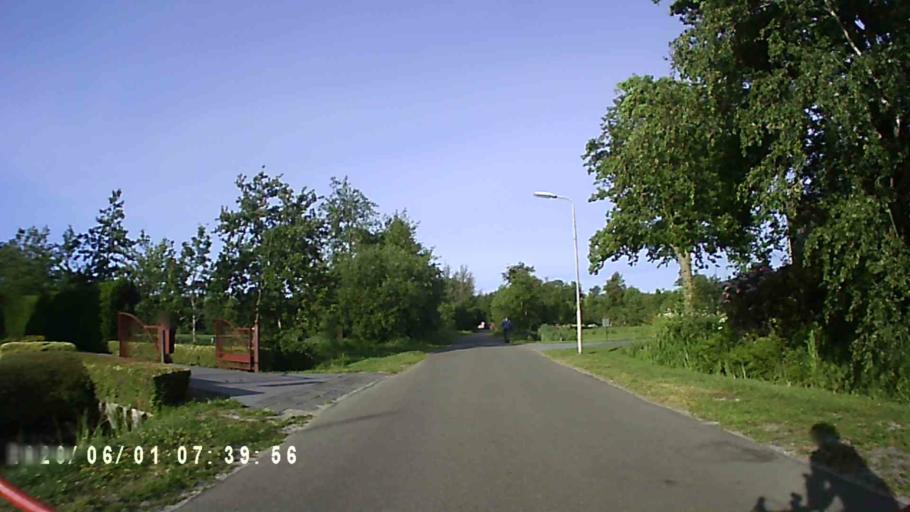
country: NL
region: Friesland
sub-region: Gemeente Dantumadiel
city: Damwald
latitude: 53.2954
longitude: 5.9905
